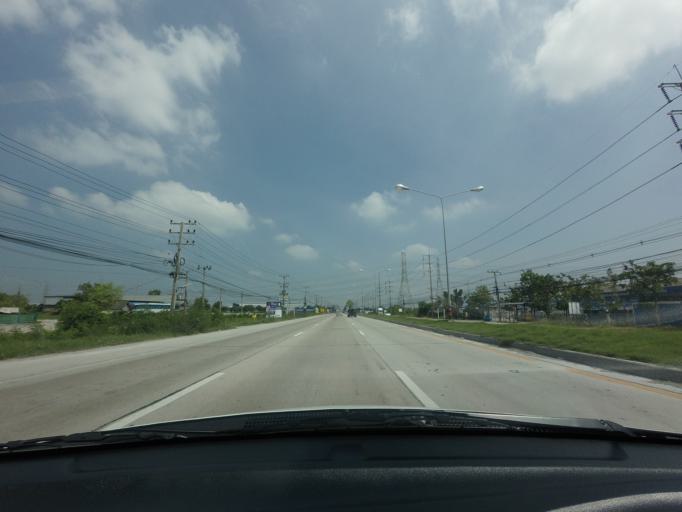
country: TH
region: Chachoengsao
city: Bang Pakong
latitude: 13.5644
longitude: 100.9975
